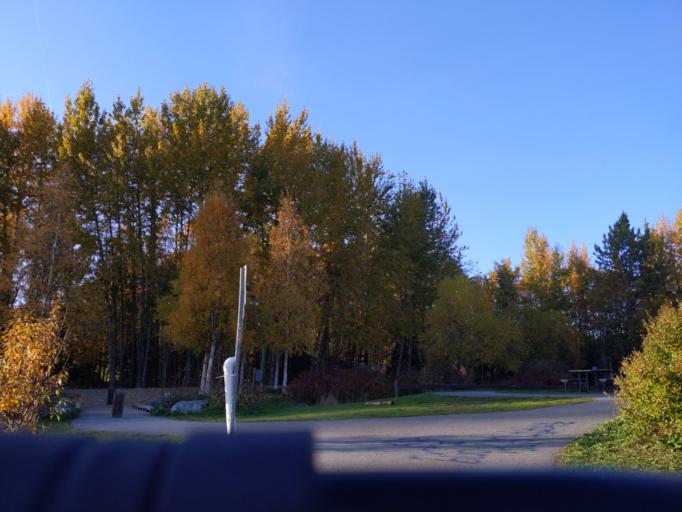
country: US
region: Alaska
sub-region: Anchorage Municipality
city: Anchorage
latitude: 61.1515
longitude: -149.8803
